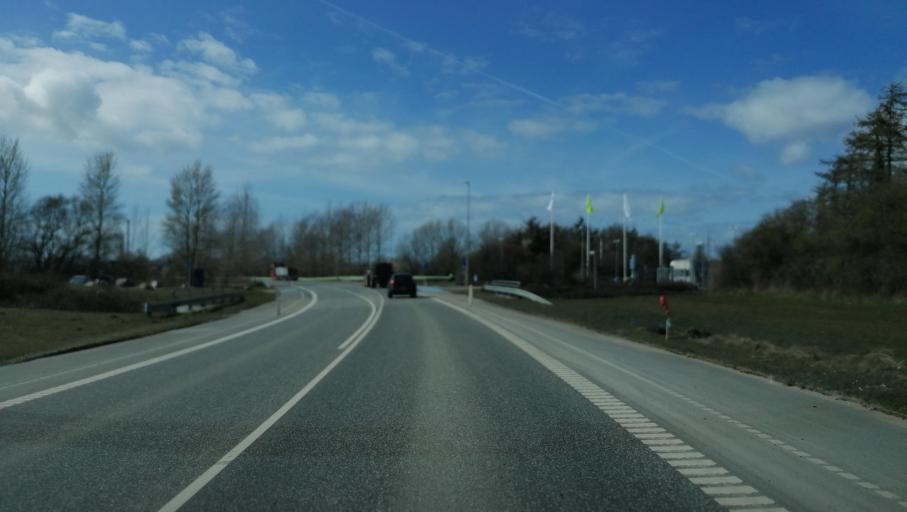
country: DK
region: Zealand
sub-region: Kalundborg Kommune
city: Kalundborg
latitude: 55.6704
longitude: 11.1223
